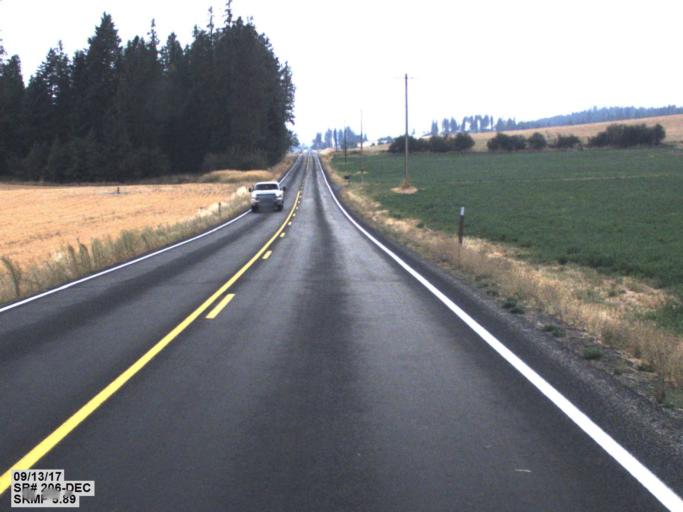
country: US
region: Washington
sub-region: Spokane County
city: Trentwood
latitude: 47.8012
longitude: -117.2363
